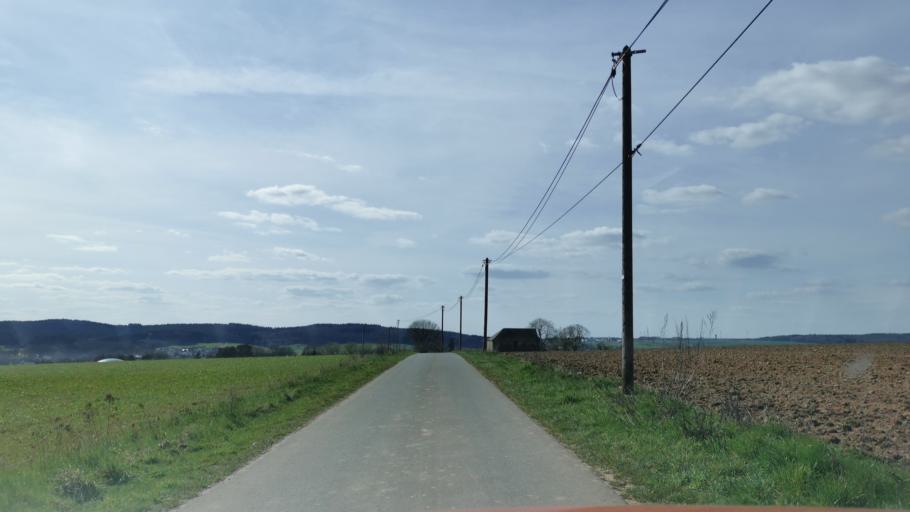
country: DE
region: Rheinland-Pfalz
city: Landscheid
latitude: 49.9604
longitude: 6.7613
